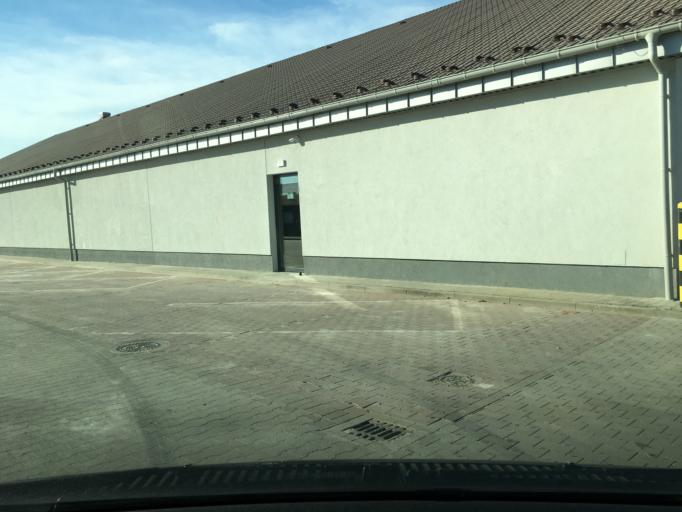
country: PL
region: Lower Silesian Voivodeship
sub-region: Powiat strzelinski
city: Strzelin
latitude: 50.7870
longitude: 17.0710
